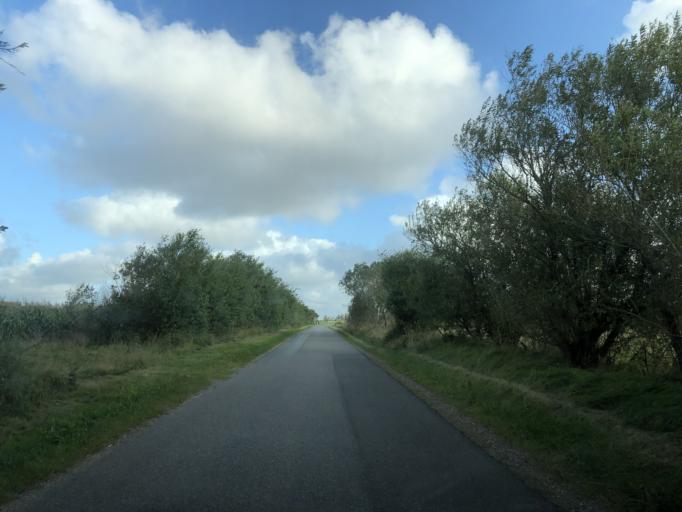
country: DK
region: Central Jutland
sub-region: Holstebro Kommune
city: Ulfborg
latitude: 56.3805
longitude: 8.3465
